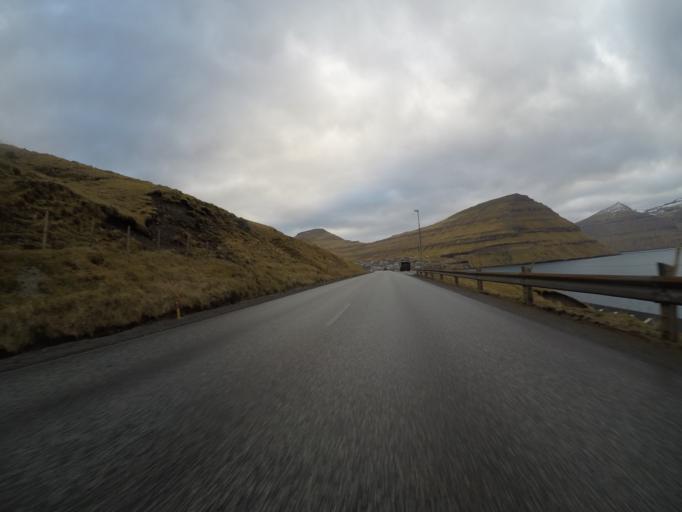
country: FO
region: Nordoyar
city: Klaksvik
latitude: 62.2460
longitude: -6.5866
